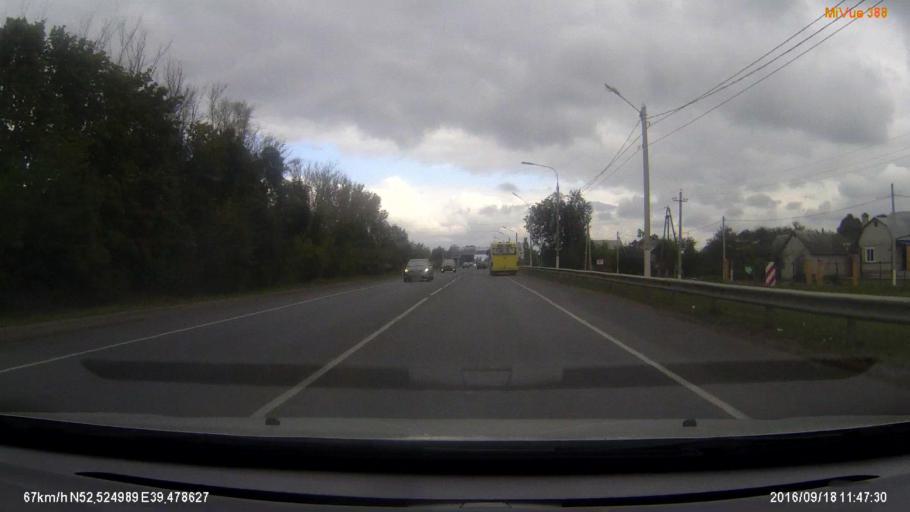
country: RU
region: Lipetsk
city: Syrskoye
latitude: 52.5249
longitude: 39.4785
